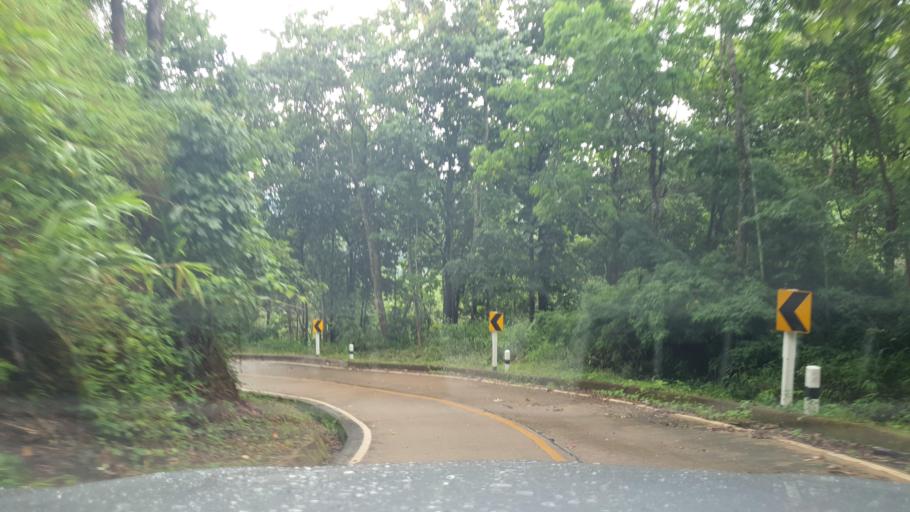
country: TH
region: Chiang Mai
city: Samoeng
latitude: 18.8395
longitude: 98.7801
